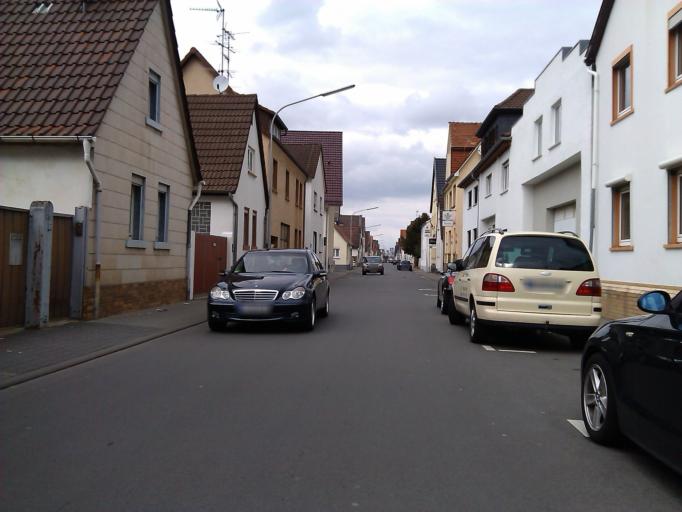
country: DE
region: Hesse
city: Griesheim
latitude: 49.8611
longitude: 8.5576
